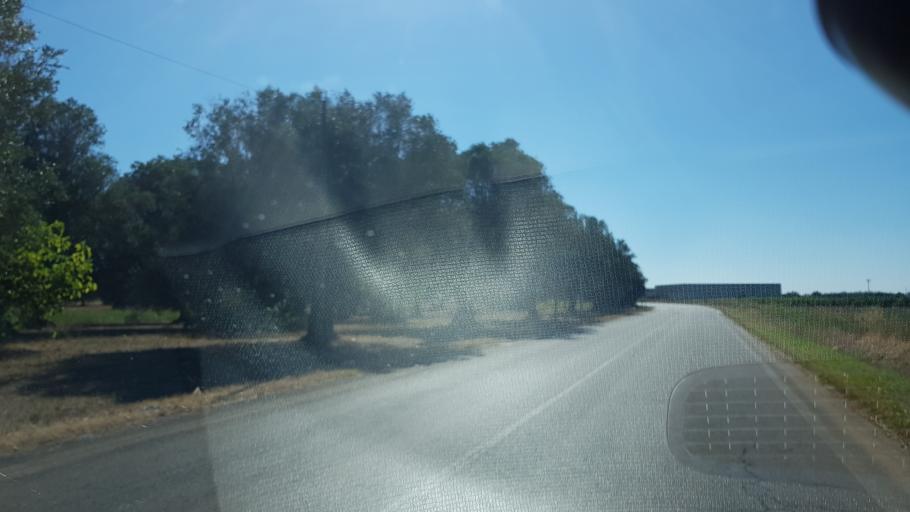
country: IT
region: Apulia
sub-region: Provincia di Brindisi
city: Mesagne
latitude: 40.5576
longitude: 17.8366
